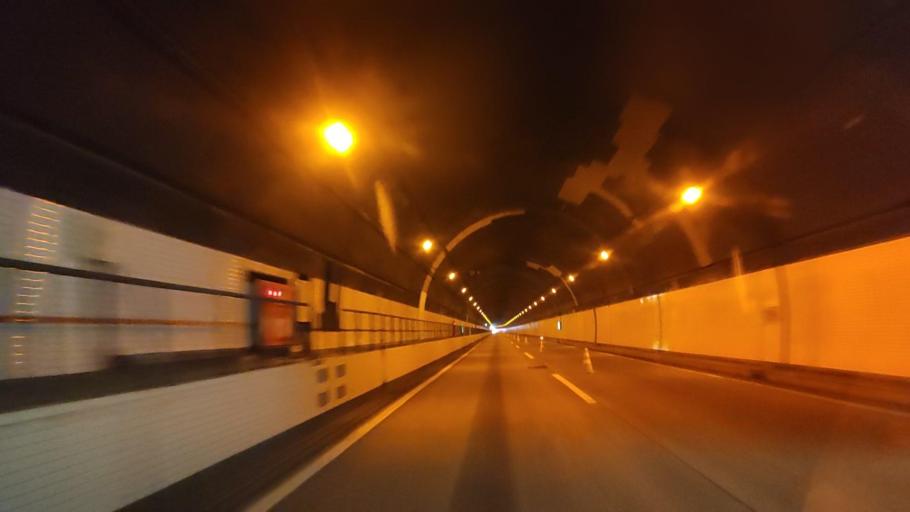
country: JP
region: Niigata
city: Itoigawa
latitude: 36.9902
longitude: 137.6961
